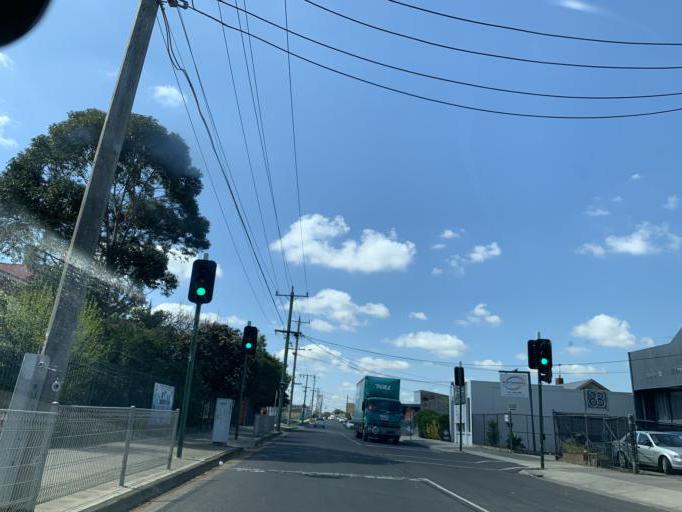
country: AU
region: Victoria
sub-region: Moreland
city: Coburg North
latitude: -37.7268
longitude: 144.9584
